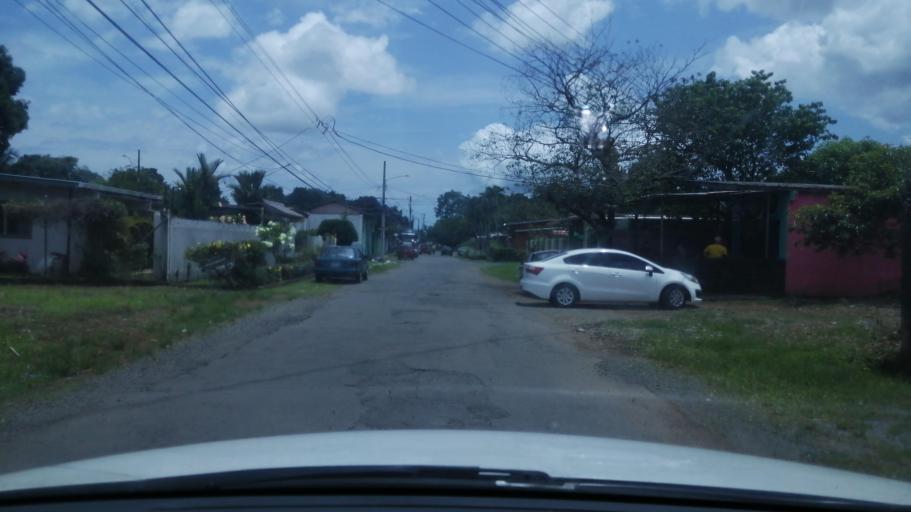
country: PA
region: Chiriqui
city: David
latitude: 8.4238
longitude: -82.4244
